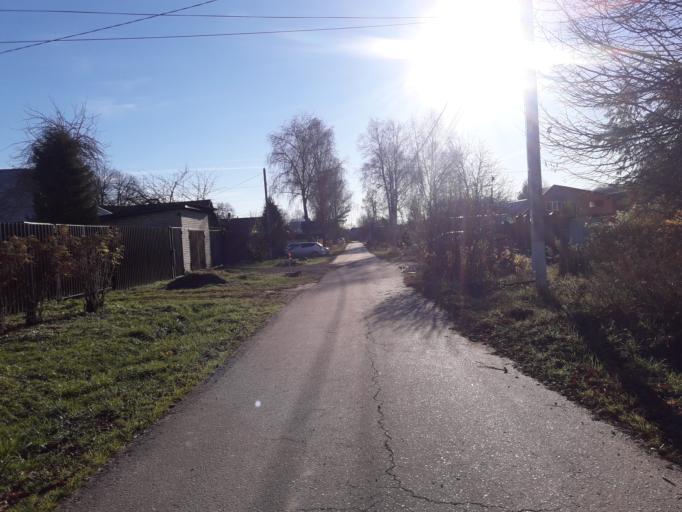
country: RU
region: Moskovskaya
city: Ashukino
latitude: 56.1653
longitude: 37.9655
